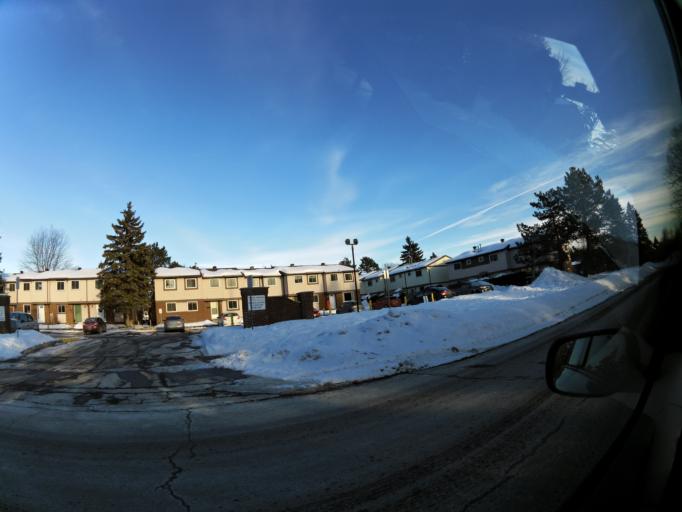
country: CA
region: Ontario
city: Ottawa
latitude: 45.4325
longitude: -75.5598
